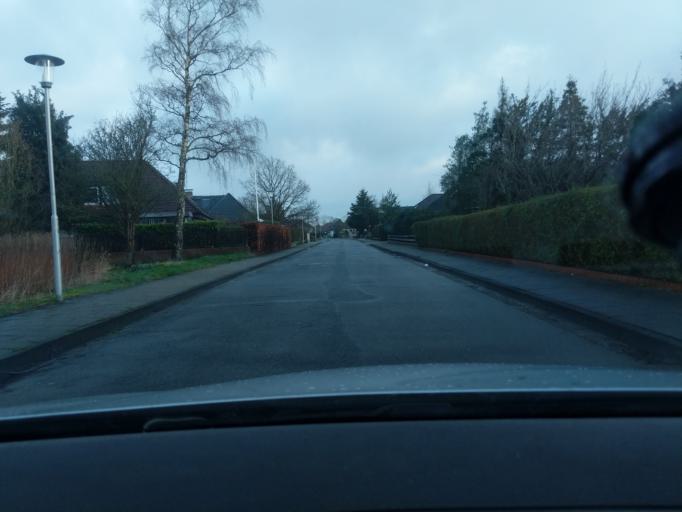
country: DE
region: Lower Saxony
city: Cuxhaven
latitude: 53.8565
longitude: 8.6825
